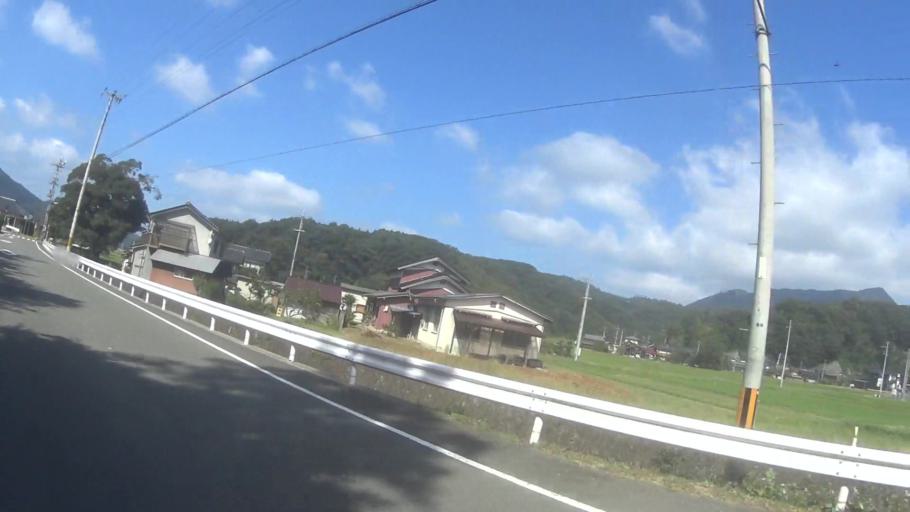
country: JP
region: Kyoto
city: Miyazu
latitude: 35.7130
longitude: 135.1147
